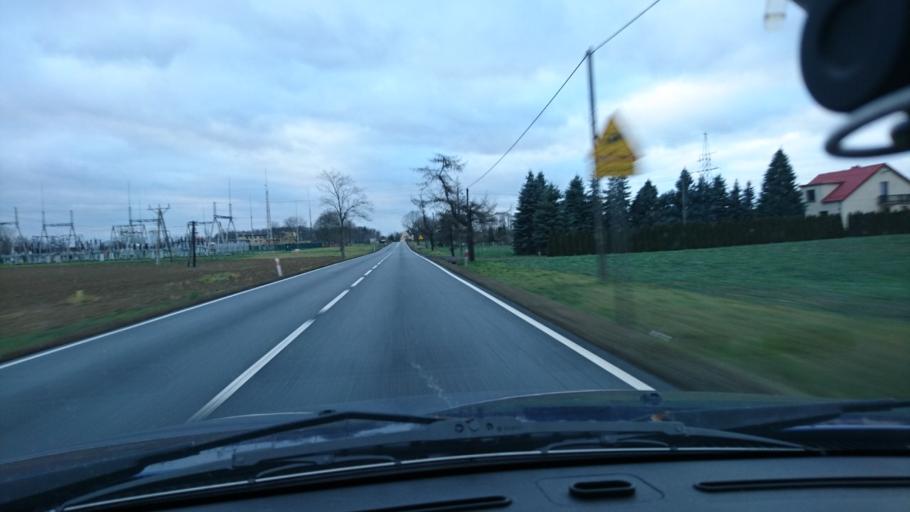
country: PL
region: Lodz Voivodeship
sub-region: Powiat wieruszowski
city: Boleslawiec
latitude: 51.1611
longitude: 18.1597
